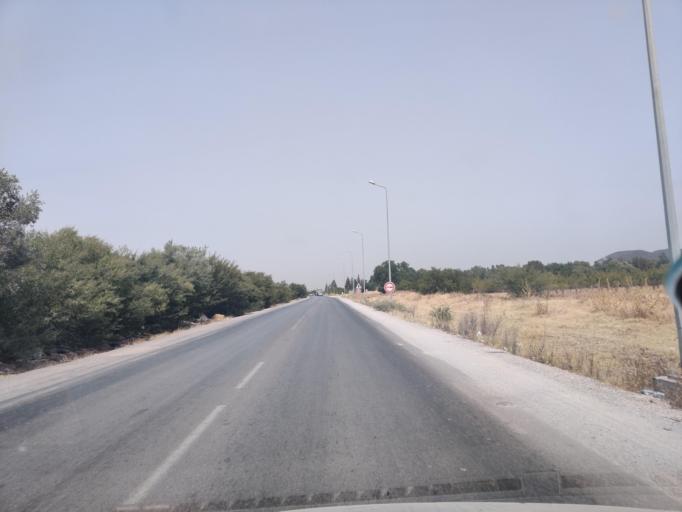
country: TN
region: Tunis
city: La Sebala du Mornag
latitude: 36.6729
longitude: 10.3195
